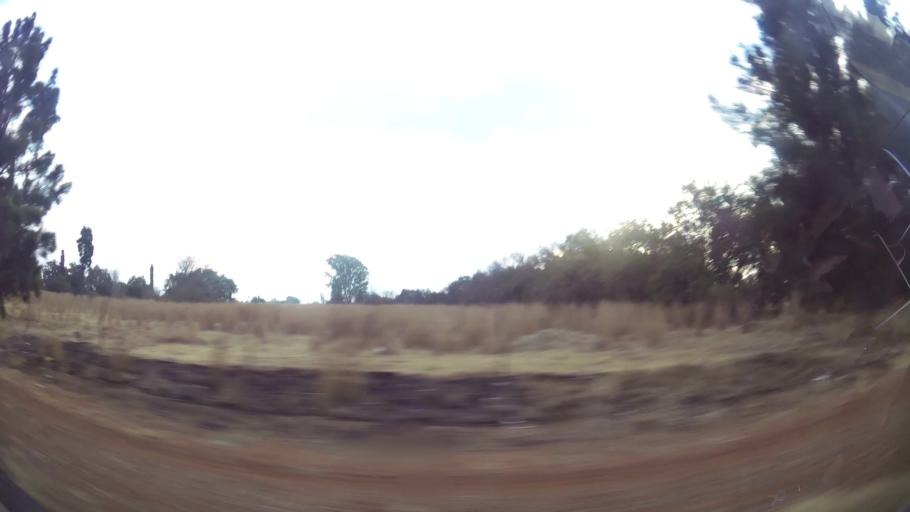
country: ZA
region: Gauteng
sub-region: Sedibeng District Municipality
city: Vanderbijlpark
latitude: -26.6363
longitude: 27.8071
